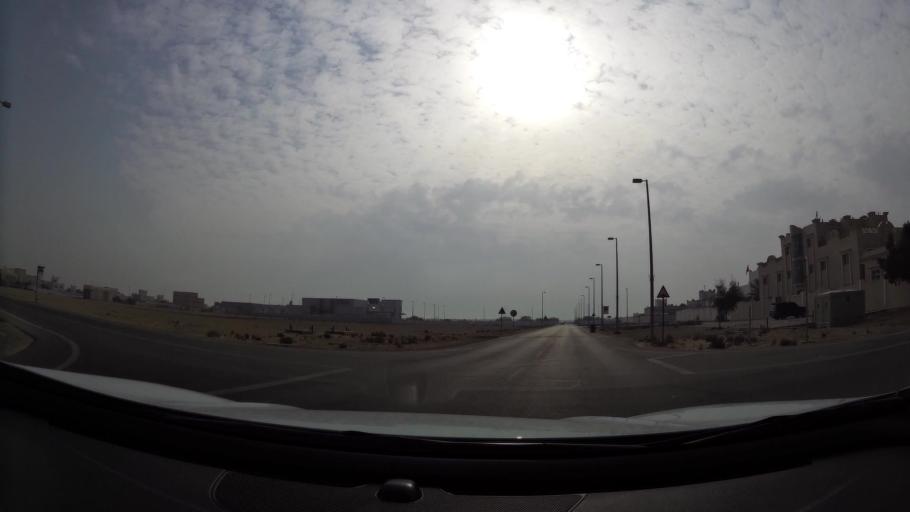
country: AE
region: Abu Dhabi
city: Abu Dhabi
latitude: 24.6657
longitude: 54.7705
